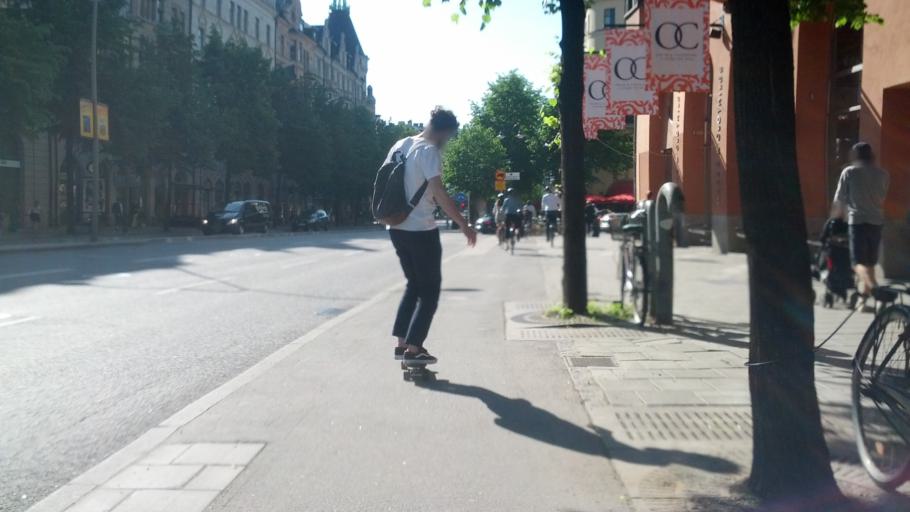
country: SE
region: Stockholm
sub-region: Stockholms Kommun
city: Stockholm
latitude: 59.3375
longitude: 18.0703
